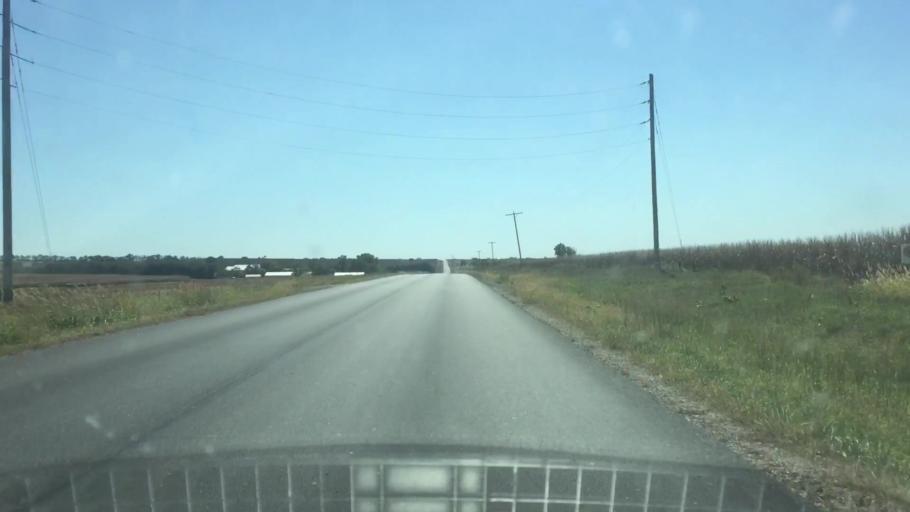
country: US
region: Kansas
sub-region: Marshall County
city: Marysville
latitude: 39.9069
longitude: -96.6010
